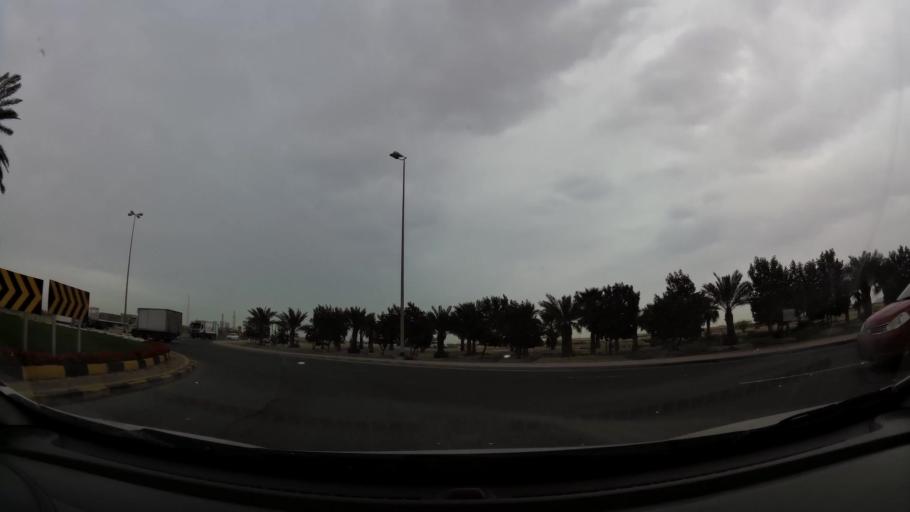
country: BH
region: Central Governorate
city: Dar Kulayb
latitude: 26.0788
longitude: 50.5398
